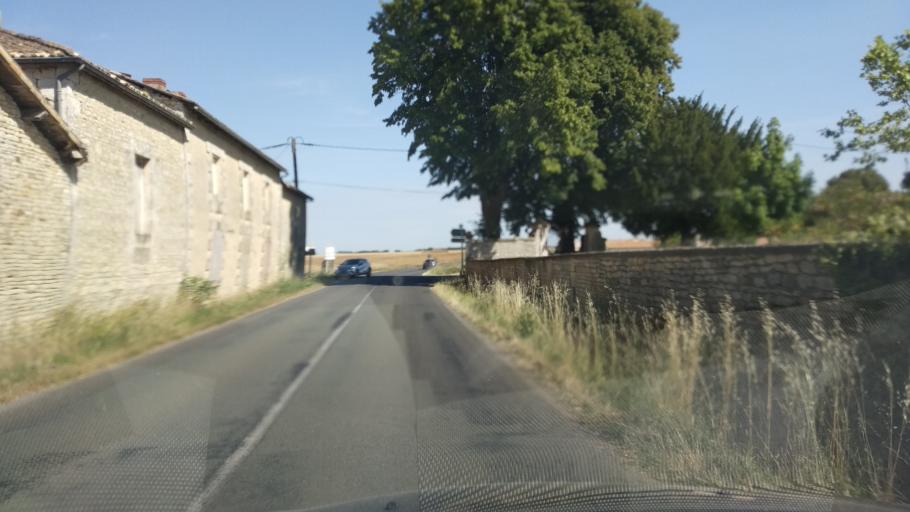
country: FR
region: Poitou-Charentes
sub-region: Departement de la Vienne
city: Vouille
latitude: 46.6800
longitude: 0.1781
